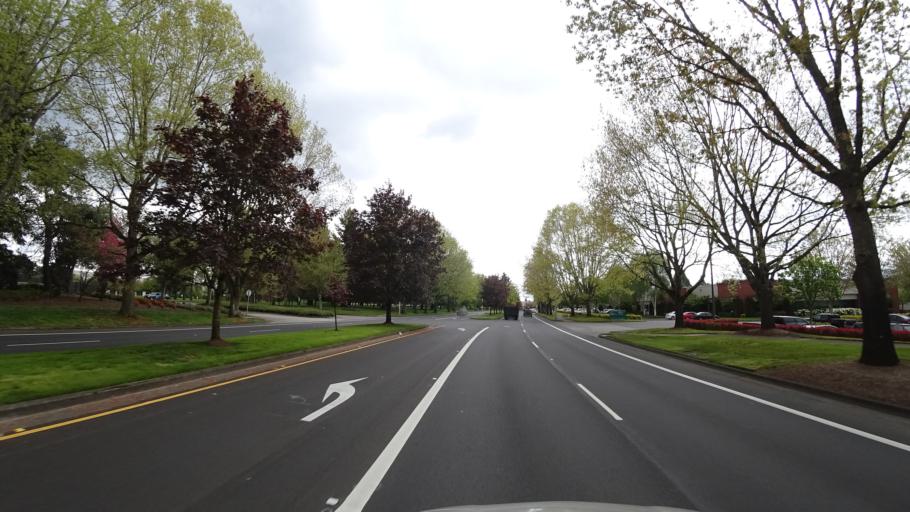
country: US
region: Oregon
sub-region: Washington County
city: Rockcreek
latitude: 45.5465
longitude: -122.9025
